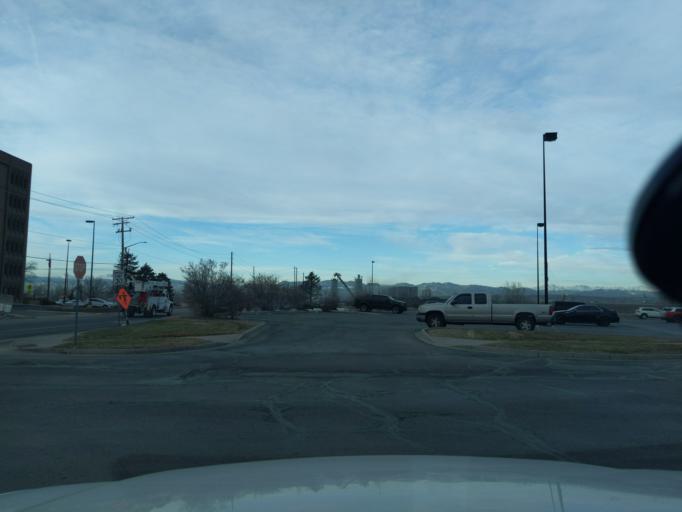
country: US
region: Colorado
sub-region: Adams County
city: Commerce City
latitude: 39.8274
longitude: -104.9380
